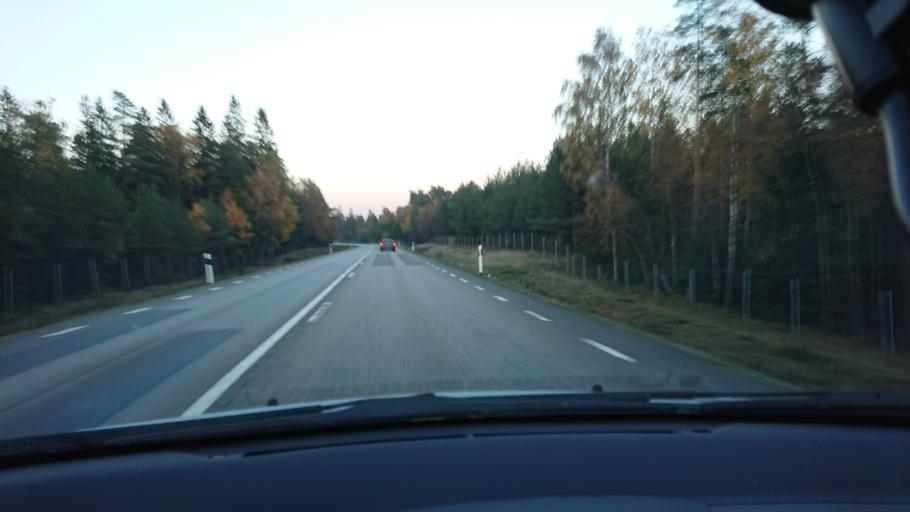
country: SE
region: Halland
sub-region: Laholms Kommun
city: Knared
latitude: 56.7289
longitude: 13.4014
